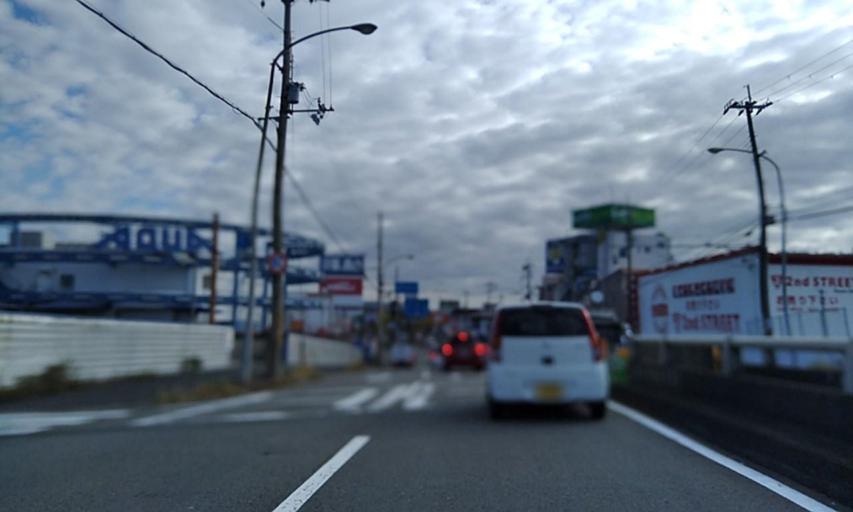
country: JP
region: Wakayama
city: Wakayama-shi
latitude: 34.2535
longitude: 135.1444
